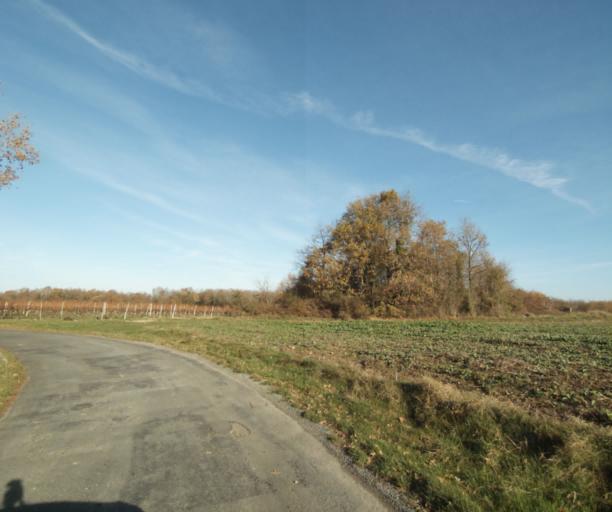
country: FR
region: Poitou-Charentes
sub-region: Departement de la Charente-Maritime
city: Cherac
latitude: 45.7515
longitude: -0.4867
